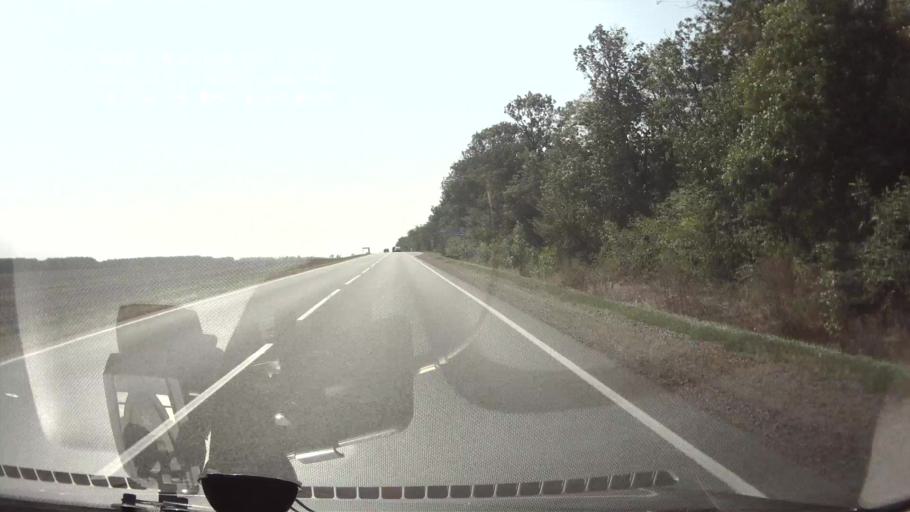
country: RU
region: Krasnodarskiy
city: Kavkazskaya
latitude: 45.5169
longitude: 40.6803
